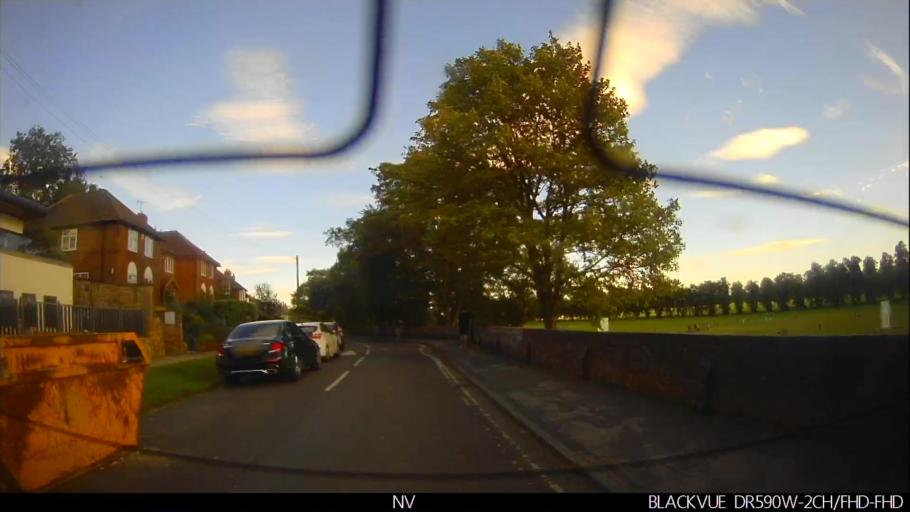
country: GB
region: England
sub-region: City of York
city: York
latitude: 53.9488
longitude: -1.0945
